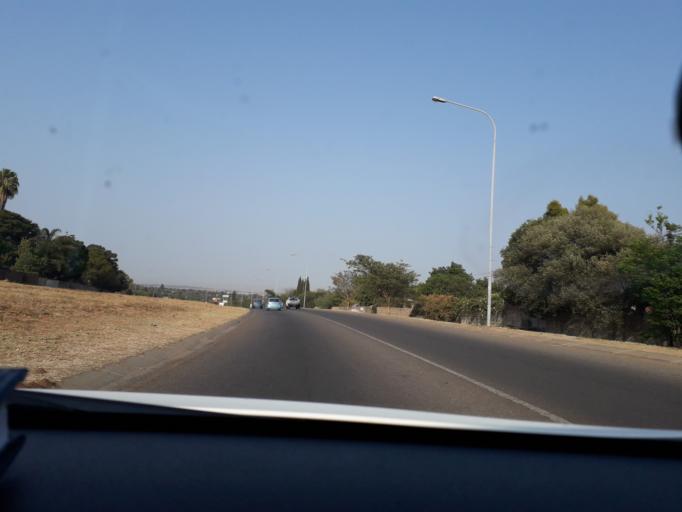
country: ZA
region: Gauteng
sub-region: City of Tshwane Metropolitan Municipality
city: Centurion
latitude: -25.8932
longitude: 28.1502
